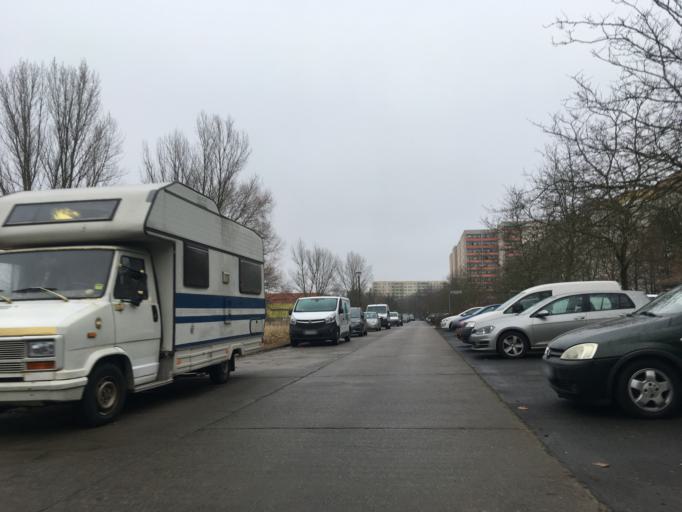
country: DE
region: Berlin
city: Buch
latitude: 52.6269
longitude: 13.4908
